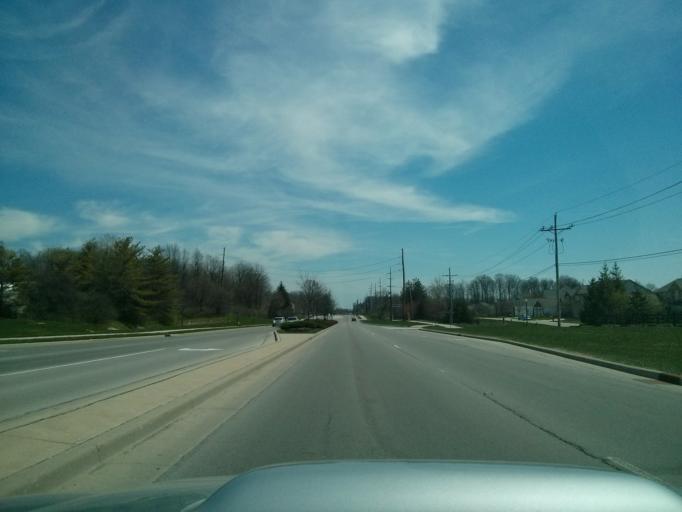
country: US
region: Indiana
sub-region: Hamilton County
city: Carmel
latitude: 39.9566
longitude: -86.1411
